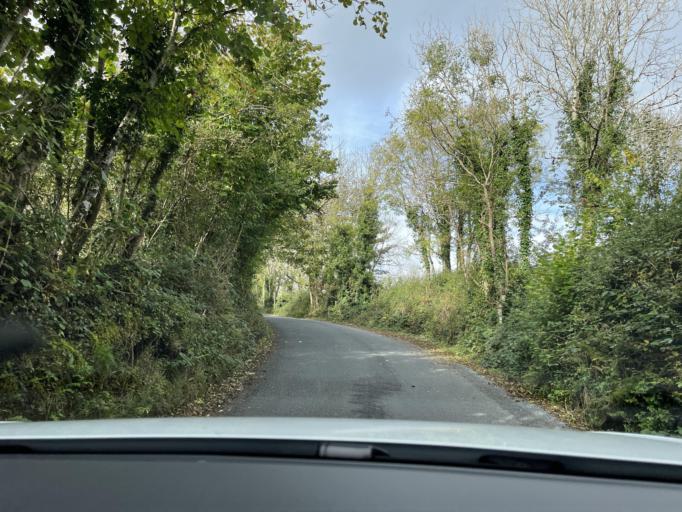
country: IE
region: Connaught
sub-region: County Leitrim
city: Carrick-on-Shannon
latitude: 53.9562
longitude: -8.0661
